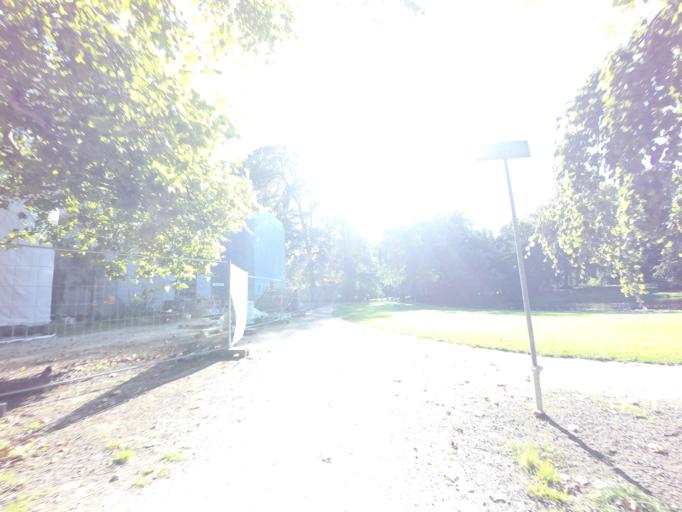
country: NL
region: South Holland
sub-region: Gemeente Wassenaar
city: Wassenaar
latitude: 52.1361
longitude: 4.3984
